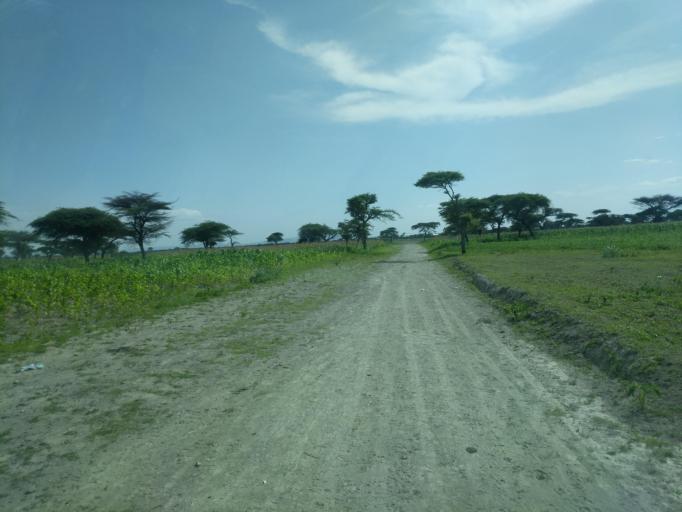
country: ET
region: Oromiya
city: Ziway
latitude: 7.6936
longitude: 38.6489
